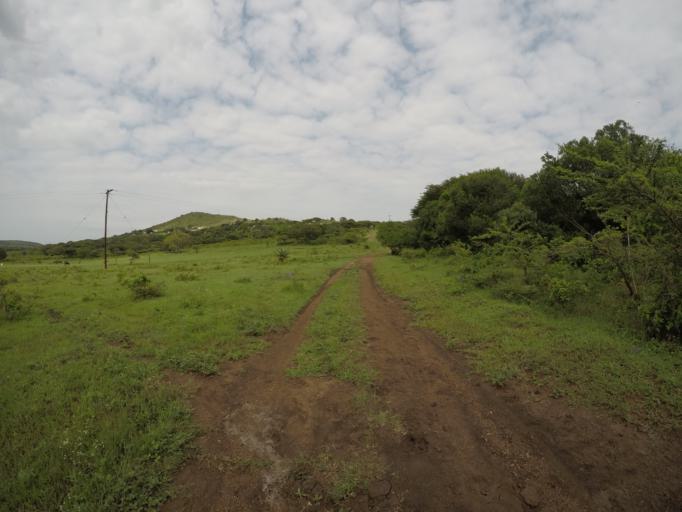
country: ZA
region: KwaZulu-Natal
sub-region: uThungulu District Municipality
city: Empangeni
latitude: -28.6256
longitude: 31.9125
